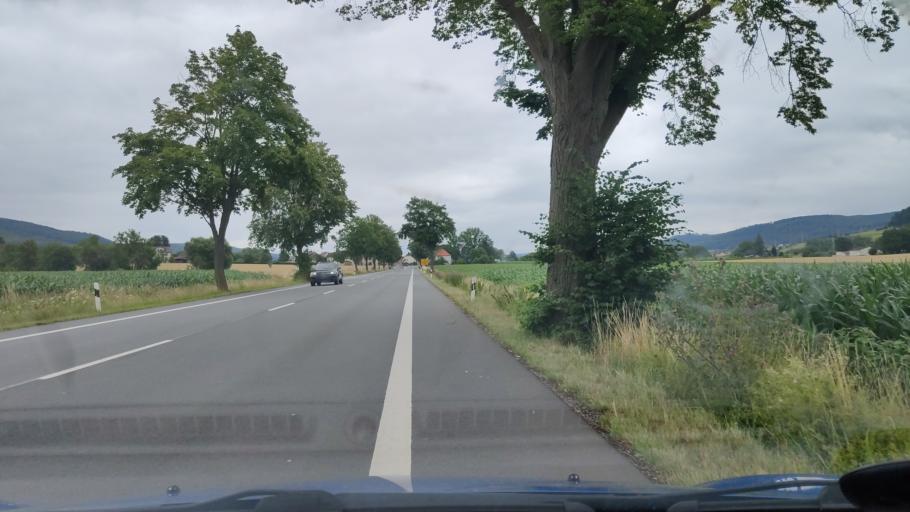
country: DE
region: Lower Saxony
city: Luerdissen
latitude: 51.9521
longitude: 9.6163
